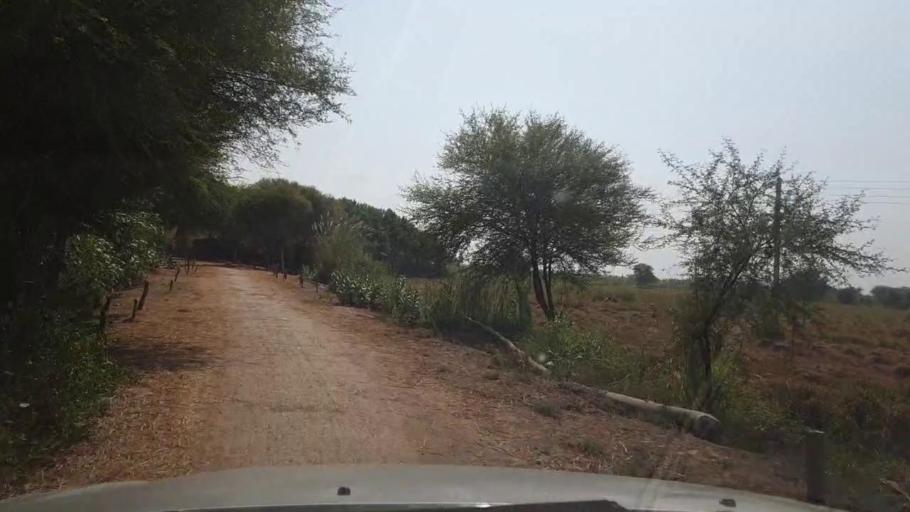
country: PK
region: Sindh
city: Bulri
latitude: 24.8813
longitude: 68.4036
